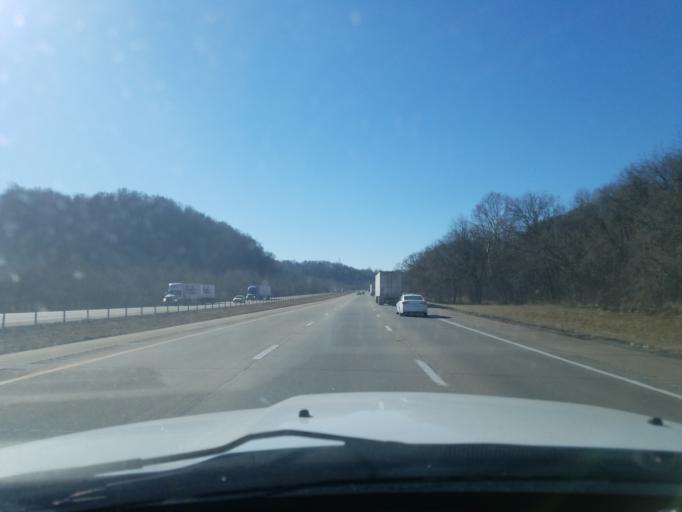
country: US
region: Kentucky
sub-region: Bullitt County
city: Lebanon Junction
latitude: 37.7782
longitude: -85.7754
